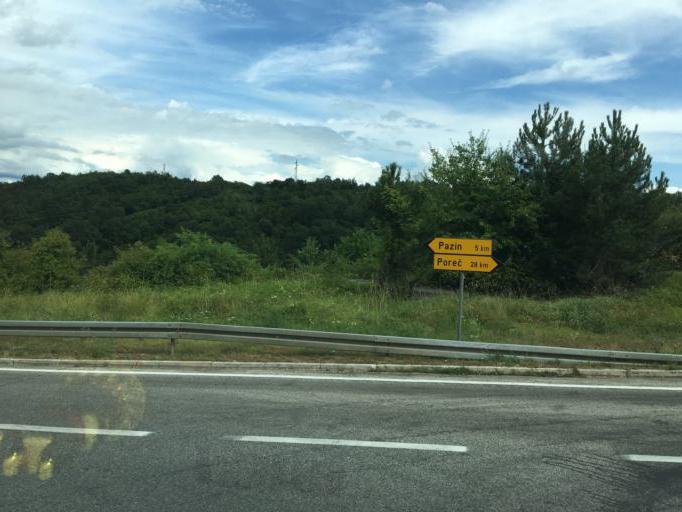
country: HR
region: Istarska
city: Pazin
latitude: 45.2497
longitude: 13.8812
